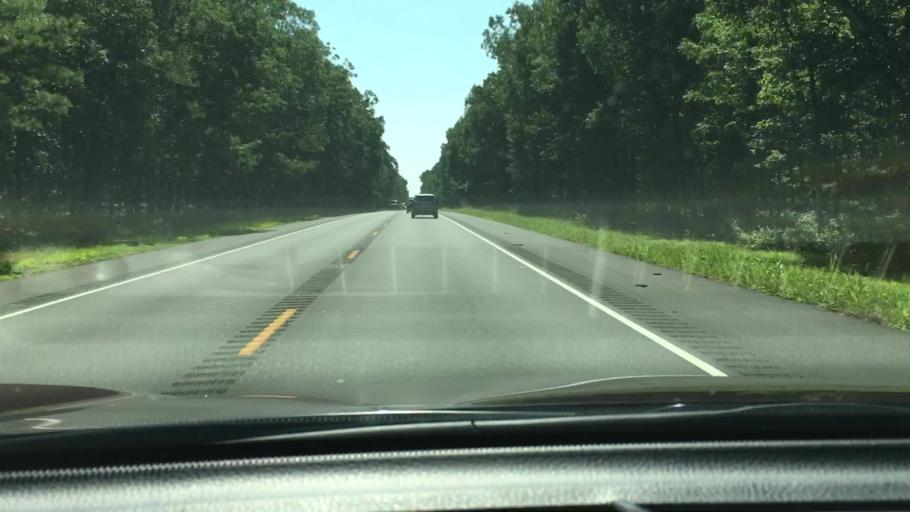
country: US
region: New Jersey
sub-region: Cape May County
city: Woodbine
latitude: 39.3362
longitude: -74.8852
